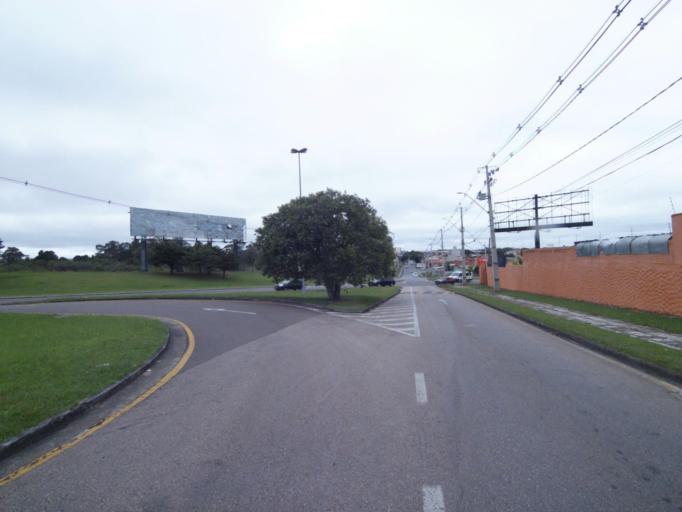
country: BR
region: Parana
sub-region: Sao Jose Dos Pinhais
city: Sao Jose dos Pinhais
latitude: -25.5369
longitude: -49.1815
